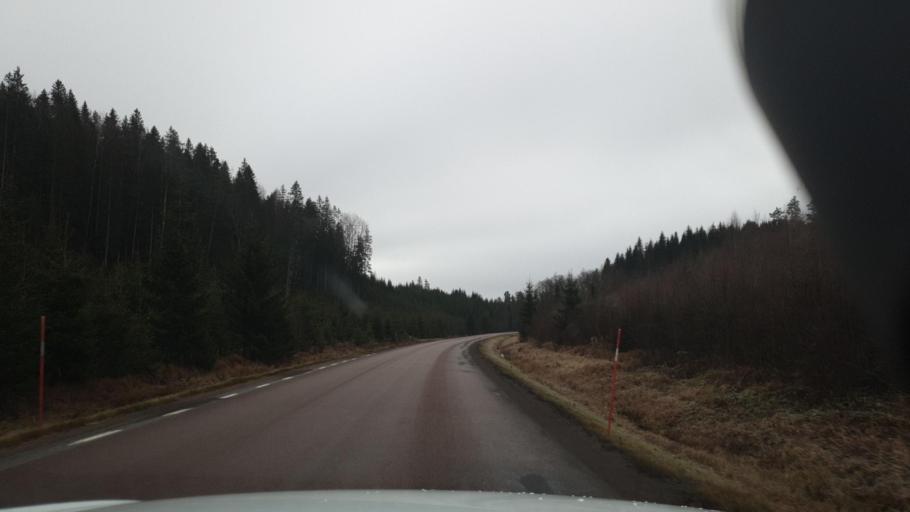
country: SE
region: Vaermland
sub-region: Arvika Kommun
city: Arvika
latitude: 59.6807
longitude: 12.7942
